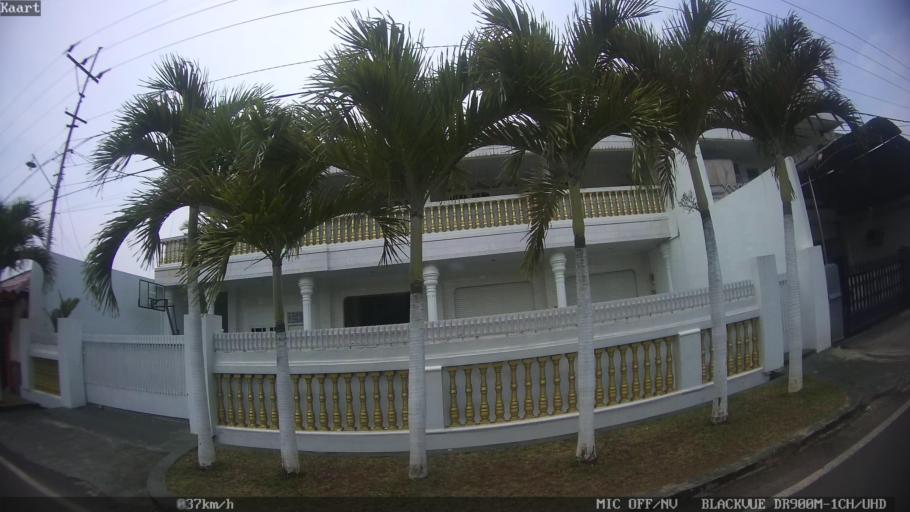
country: ID
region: Lampung
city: Bandarlampung
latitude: -5.4241
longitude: 105.2744
